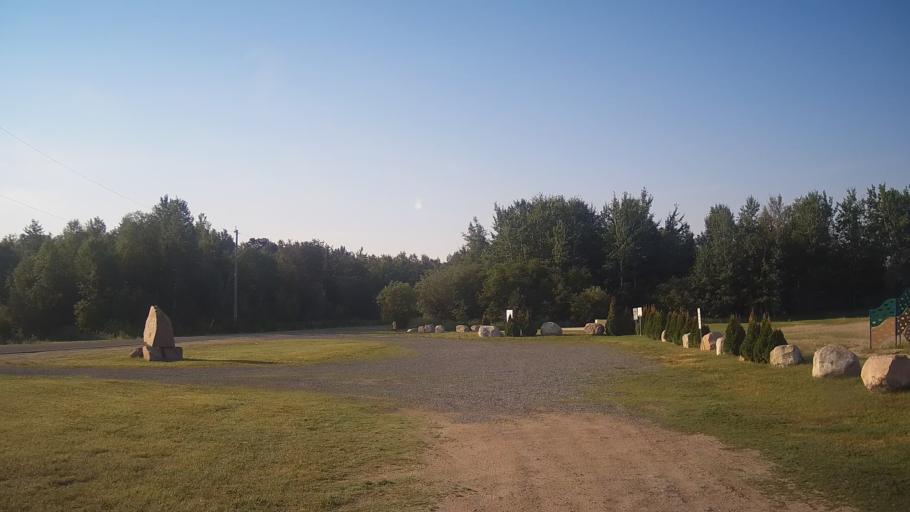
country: CA
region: Ontario
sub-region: Rainy River District
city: Atikokan
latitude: 49.4055
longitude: -91.6669
